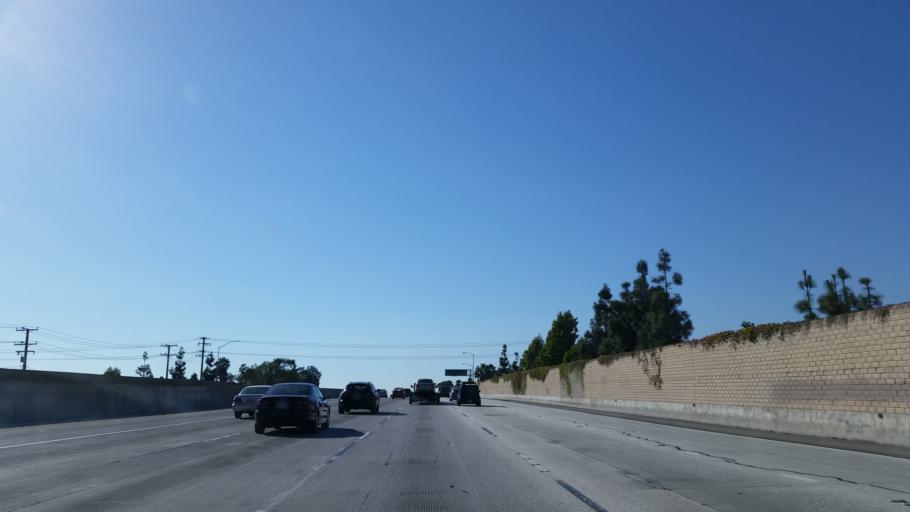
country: US
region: California
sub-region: Orange County
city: Buena Park
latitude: 33.8562
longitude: -117.9916
